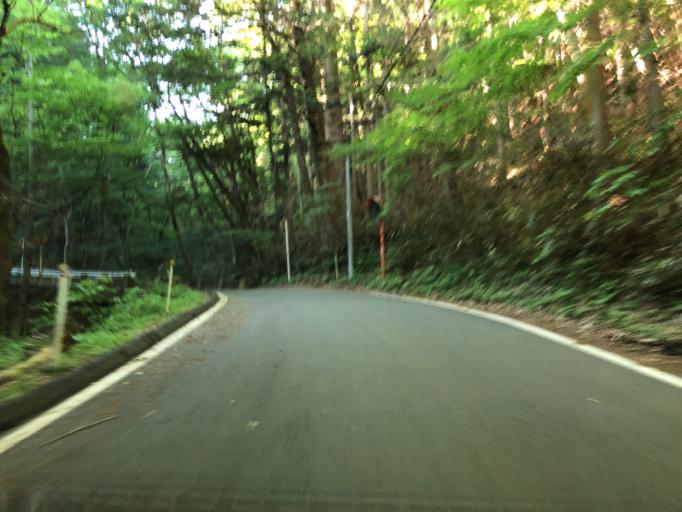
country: JP
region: Ibaraki
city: Kitaibaraki
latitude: 36.8882
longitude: 140.6238
